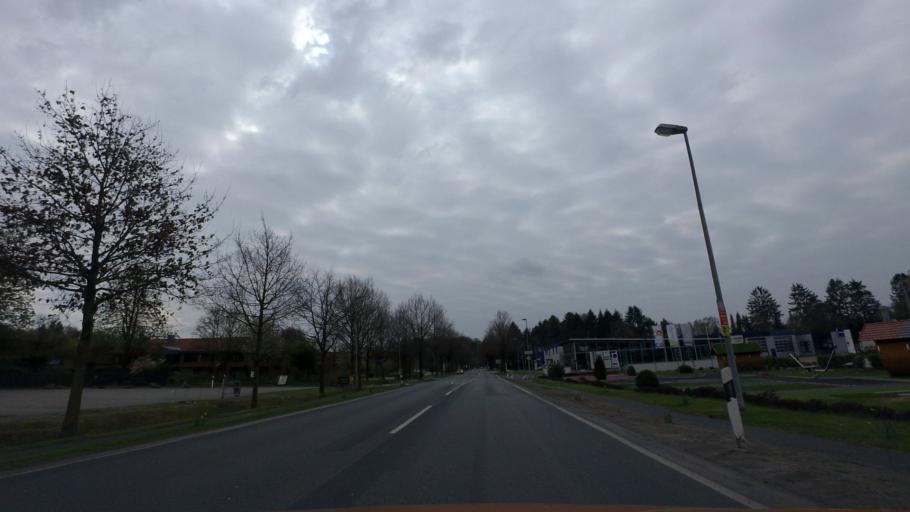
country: DE
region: Lower Saxony
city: Wildeshausen
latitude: 52.9051
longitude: 8.4427
